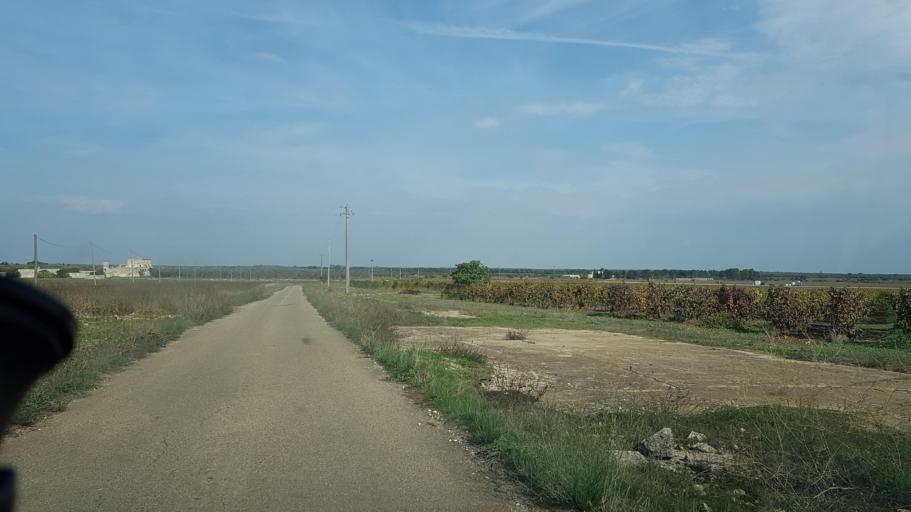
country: IT
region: Apulia
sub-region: Provincia di Brindisi
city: San Pancrazio Salentino
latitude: 40.4354
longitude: 17.8517
